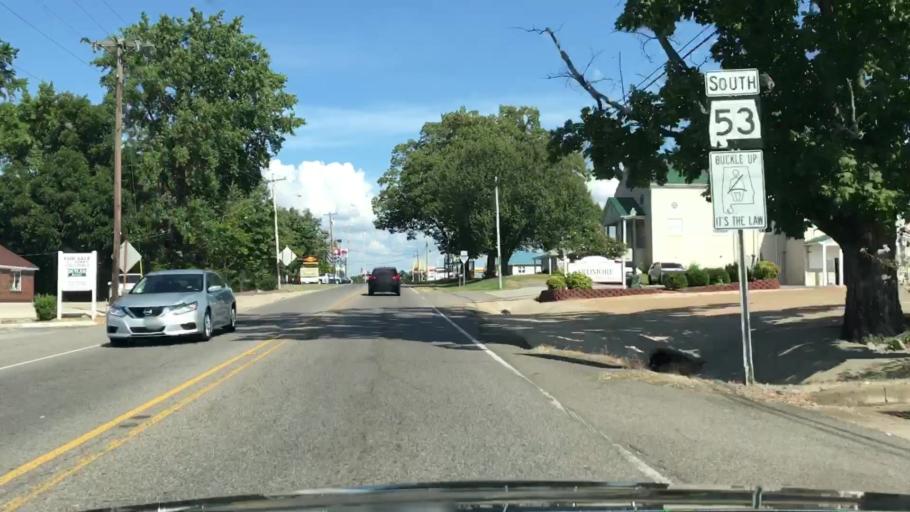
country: US
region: Tennessee
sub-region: Giles County
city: Ardmore
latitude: 34.9920
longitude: -86.8441
